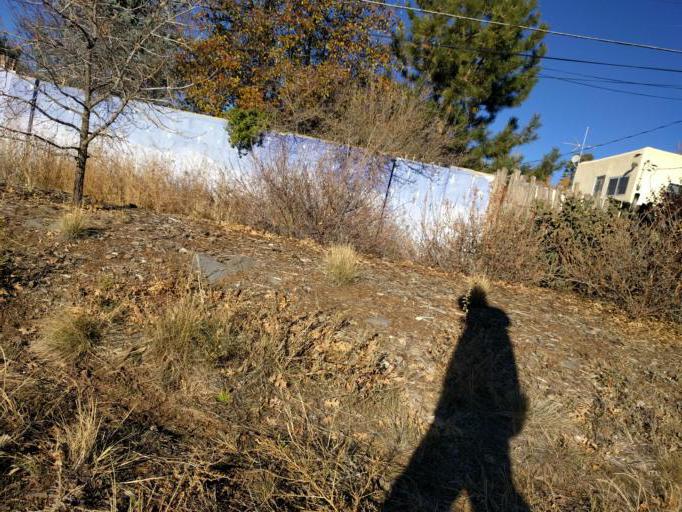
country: US
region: New Mexico
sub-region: Santa Fe County
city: Santa Fe
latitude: 35.6670
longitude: -105.9615
